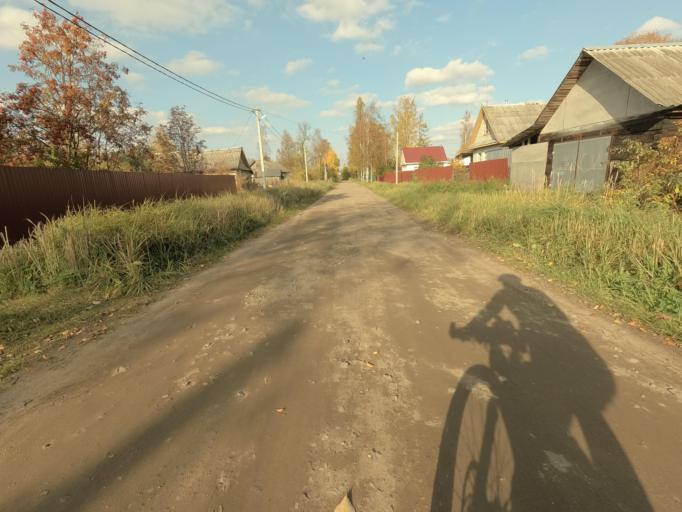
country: RU
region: Leningrad
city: Mga
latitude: 59.7508
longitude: 31.0732
